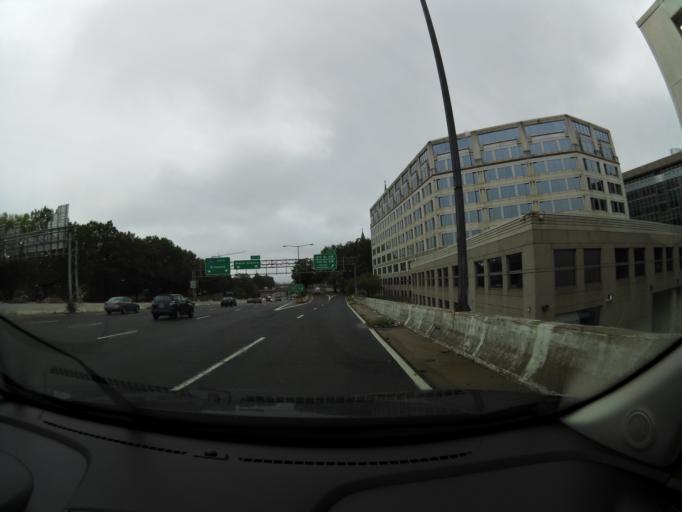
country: US
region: Washington, D.C.
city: Washington, D.C.
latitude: 38.8827
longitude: -77.0181
